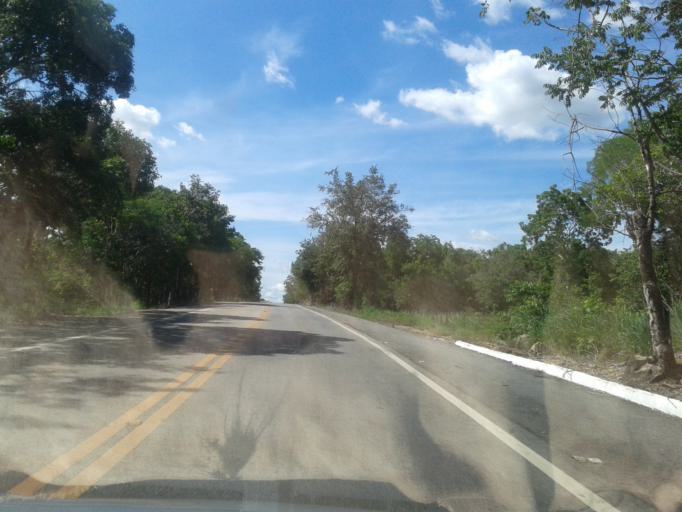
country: BR
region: Goias
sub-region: Itapuranga
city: Itapuranga
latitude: -15.4050
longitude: -50.3795
